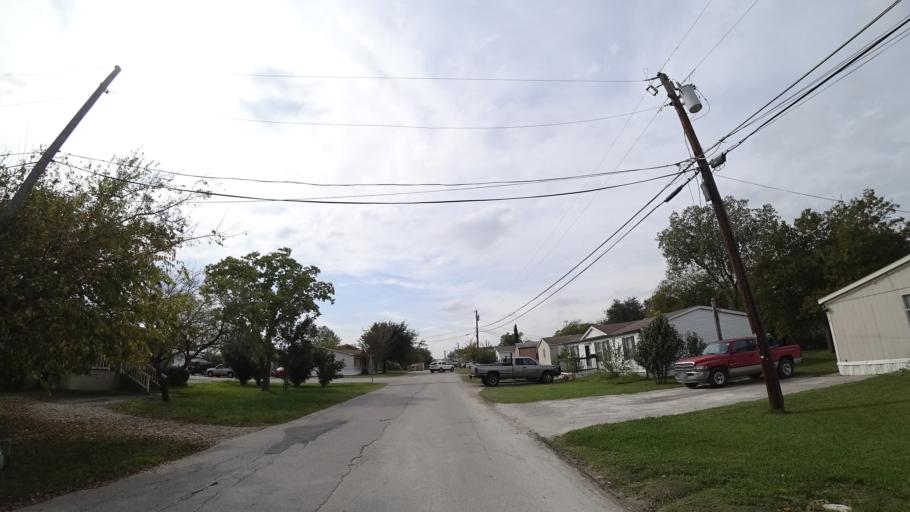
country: US
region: Texas
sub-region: Williamson County
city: Round Rock
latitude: 30.4867
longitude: -97.6900
